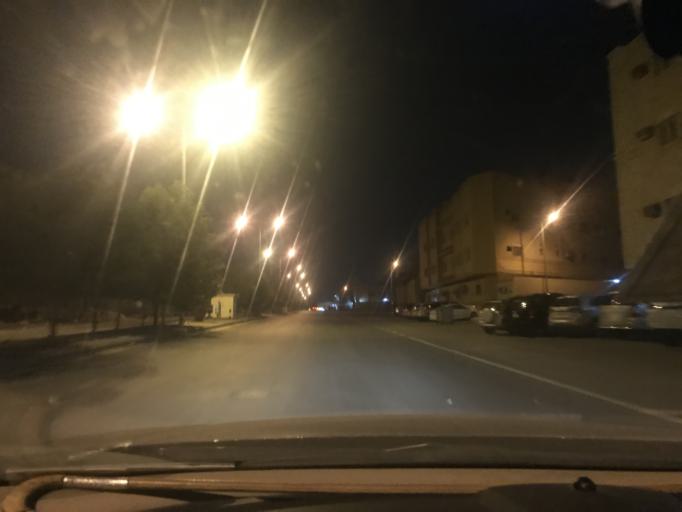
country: SA
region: Ar Riyad
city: Riyadh
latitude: 24.7499
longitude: 46.7539
